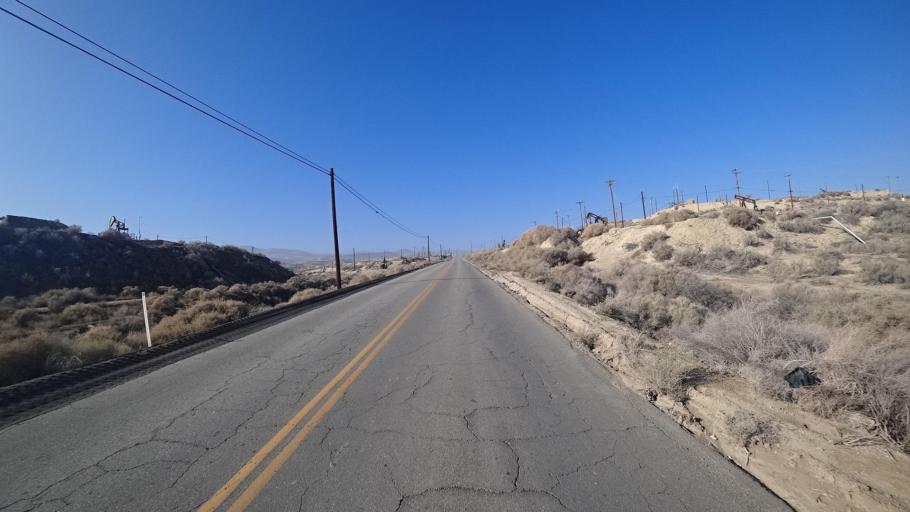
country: US
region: California
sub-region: Kern County
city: Taft Heights
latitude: 35.2196
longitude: -119.6001
